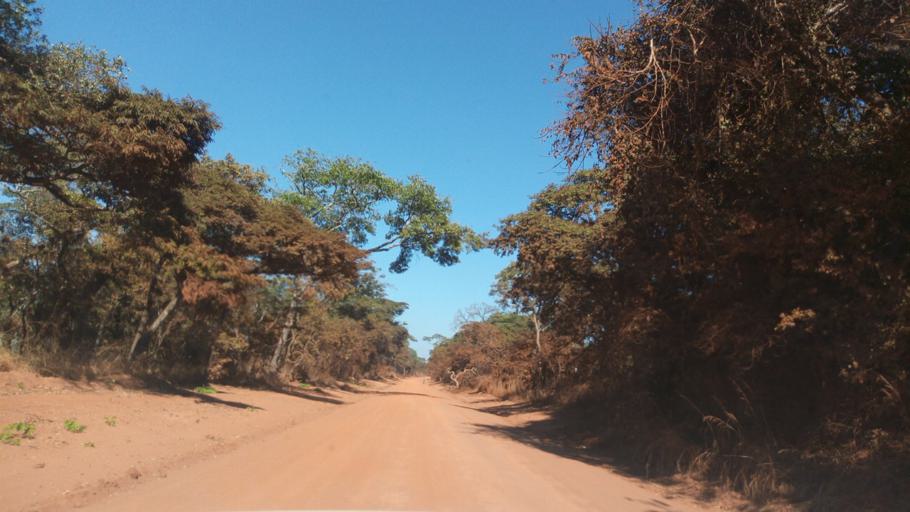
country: ZM
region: Luapula
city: Mwense
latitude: -10.7348
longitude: 28.3420
